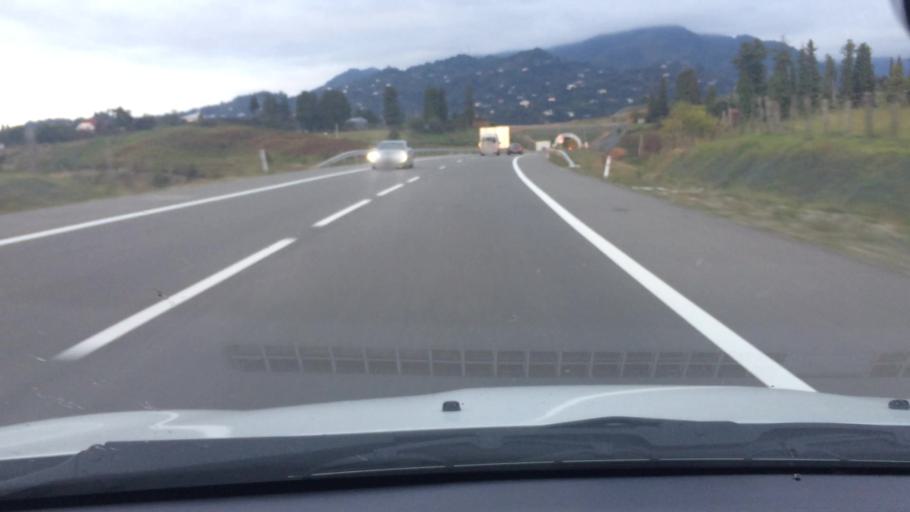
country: GE
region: Ajaria
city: Makhinjauri
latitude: 41.7072
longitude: 41.7422
